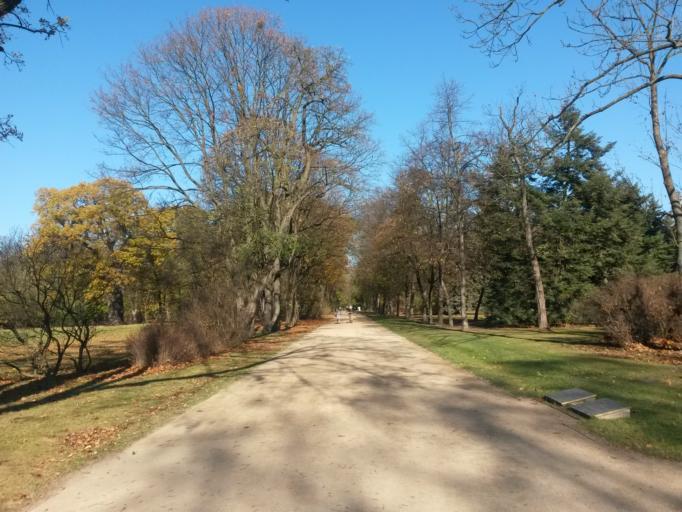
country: PL
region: Masovian Voivodeship
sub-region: Warszawa
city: Mokotow
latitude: 52.2116
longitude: 21.0328
